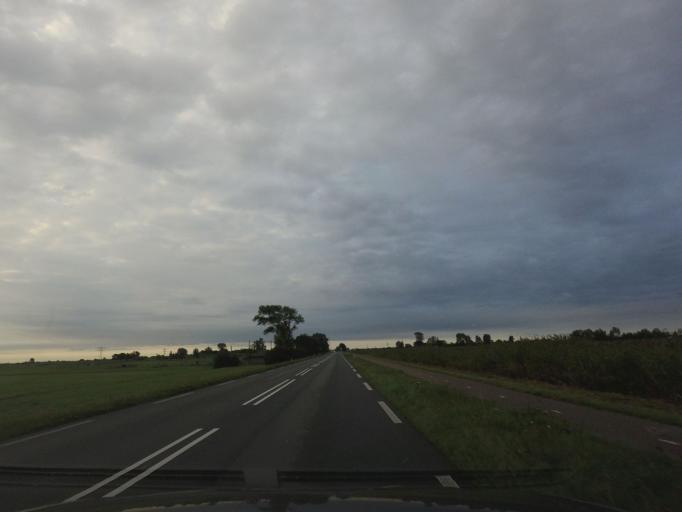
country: NL
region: North Holland
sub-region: Gemeente Uitgeest
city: Uitgeest
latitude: 52.5394
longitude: 4.7780
